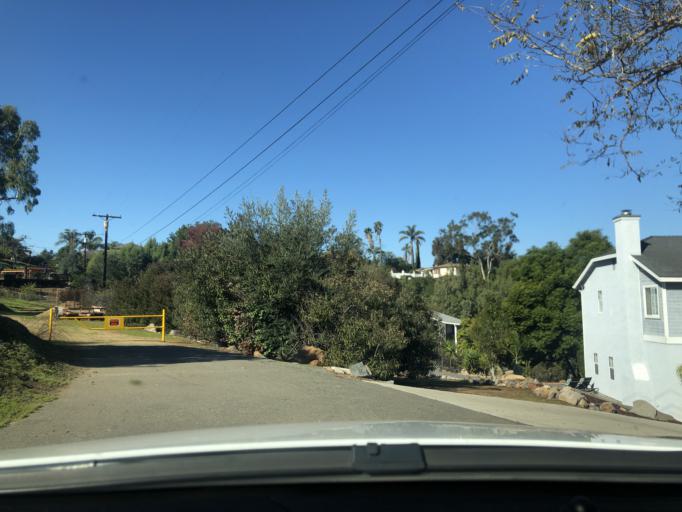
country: US
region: California
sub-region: San Diego County
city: El Cajon
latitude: 32.7760
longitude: -116.9466
